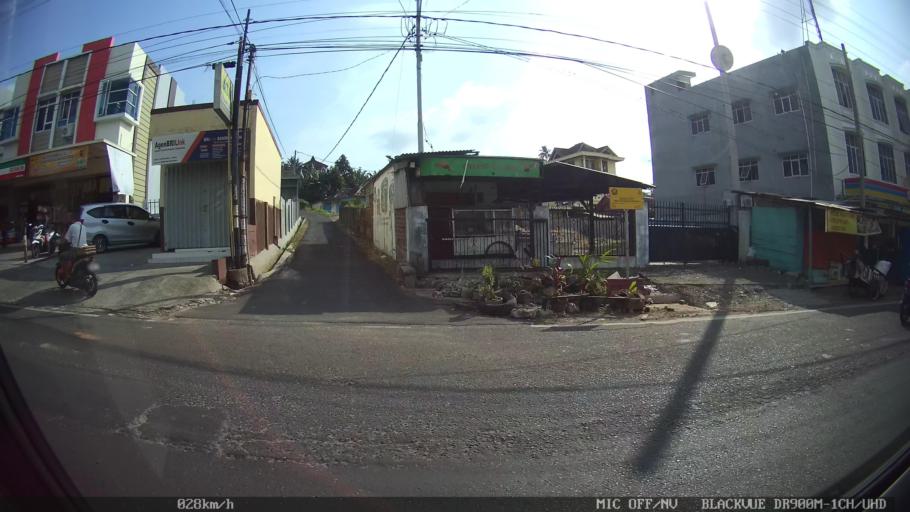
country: ID
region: Lampung
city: Bandarlampung
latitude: -5.4063
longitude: 105.2531
